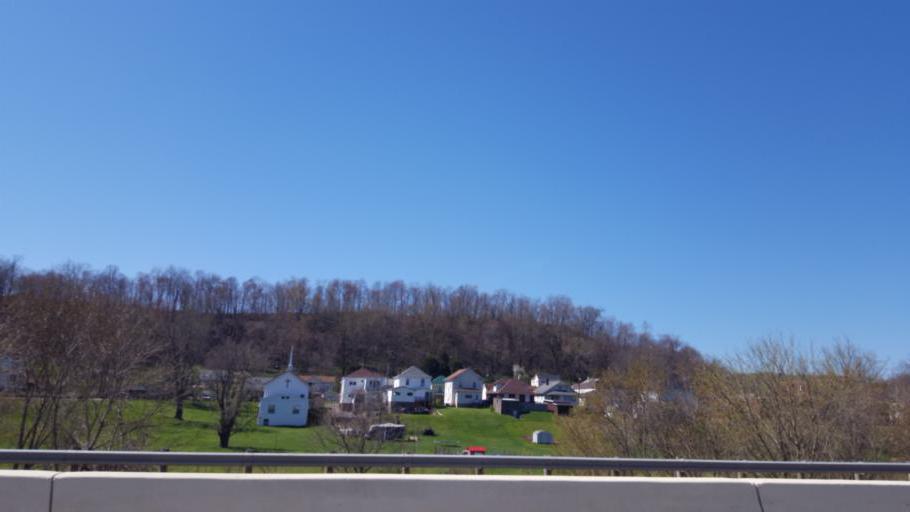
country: US
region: Ohio
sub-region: Jefferson County
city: Tiltonsville
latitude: 40.1841
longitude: -80.6886
